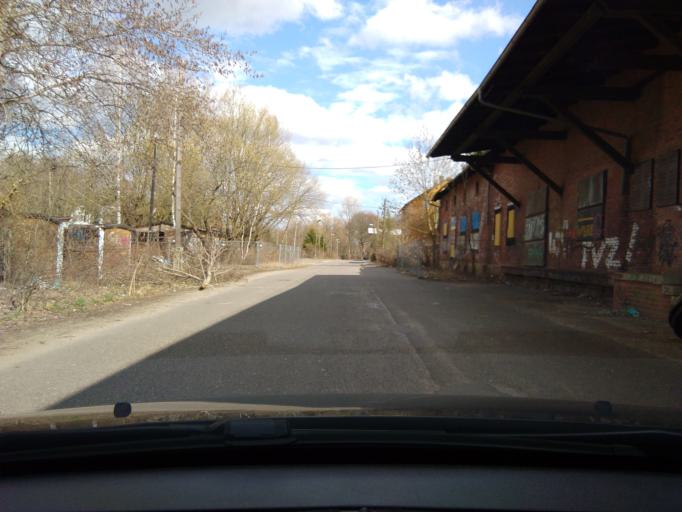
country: DE
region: Saxony
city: Chemnitz
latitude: 50.8366
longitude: 12.8863
